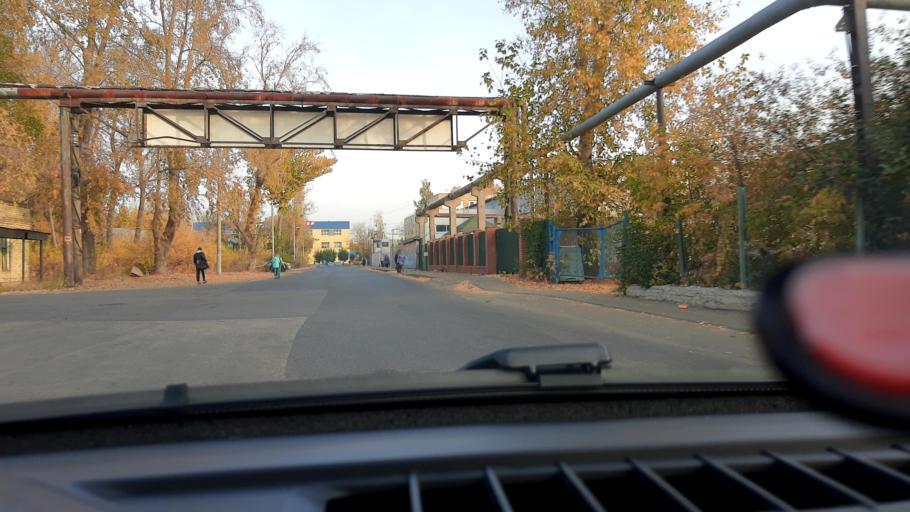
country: RU
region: Nizjnij Novgorod
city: Nizhniy Novgorod
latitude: 56.3143
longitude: 43.9127
